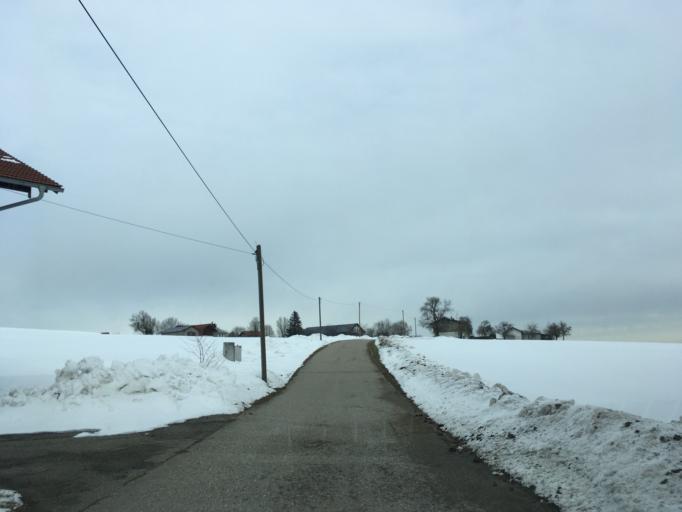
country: DE
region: Bavaria
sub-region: Upper Bavaria
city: Schnaitsee
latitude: 48.0797
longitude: 12.3749
